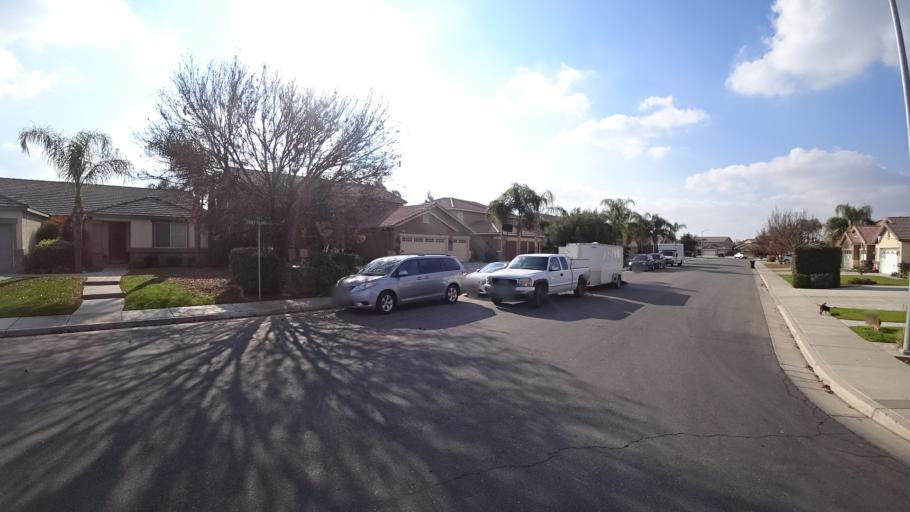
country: US
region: California
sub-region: Kern County
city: Greenacres
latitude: 35.3020
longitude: -119.1067
